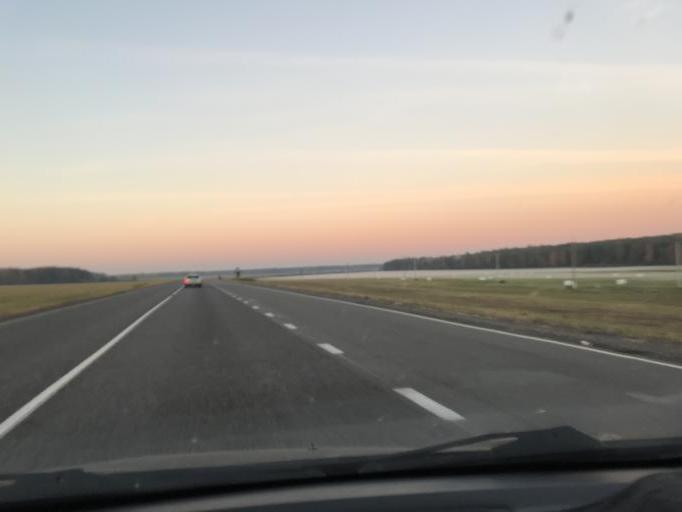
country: BY
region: Mogilev
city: Babruysk
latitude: 53.1891
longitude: 29.0511
